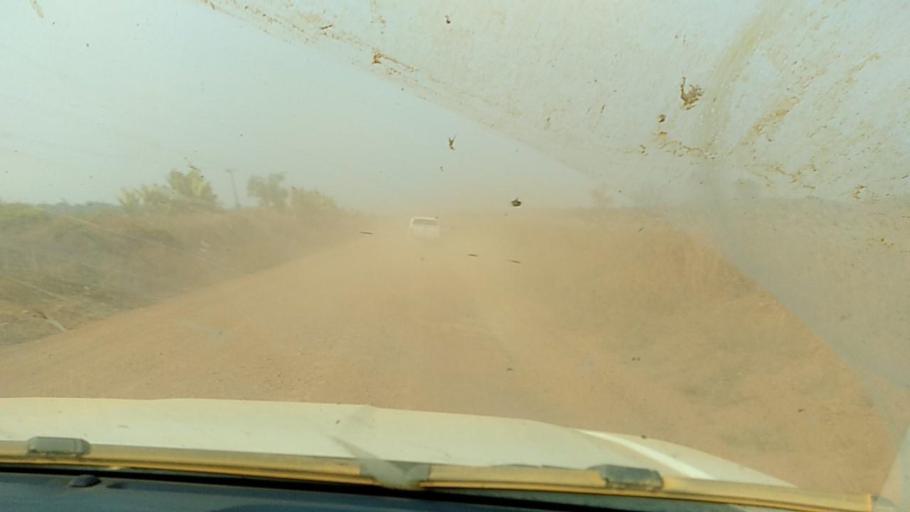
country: BR
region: Rondonia
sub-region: Porto Velho
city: Porto Velho
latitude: -8.7639
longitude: -64.0703
